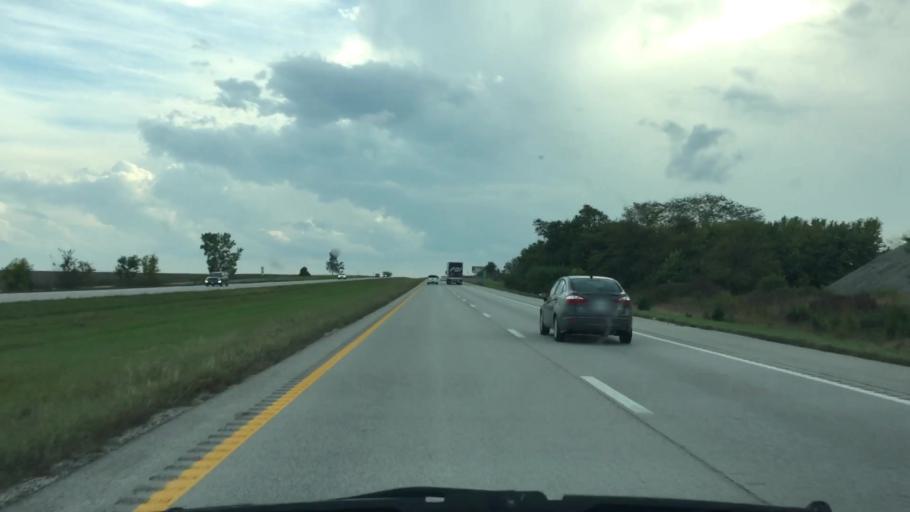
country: US
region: Missouri
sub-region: Clinton County
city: Cameron
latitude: 39.8400
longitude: -94.1830
